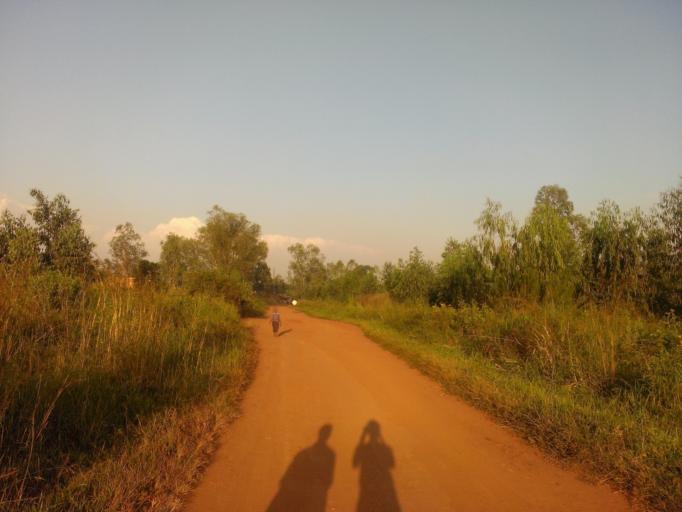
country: UG
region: Northern Region
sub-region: Gulu District
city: Gulu
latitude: 2.7829
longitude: 32.3121
